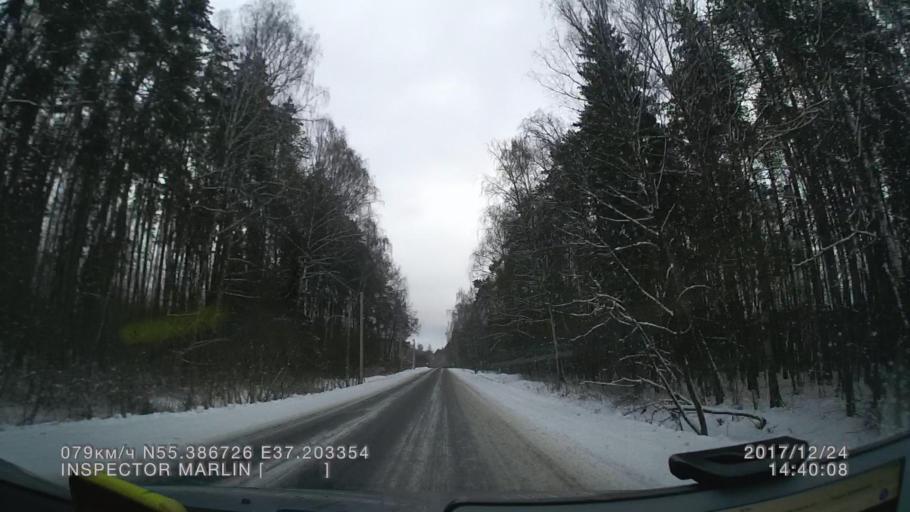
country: RU
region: Moskovskaya
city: Troitsk
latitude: 55.3866
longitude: 37.2037
